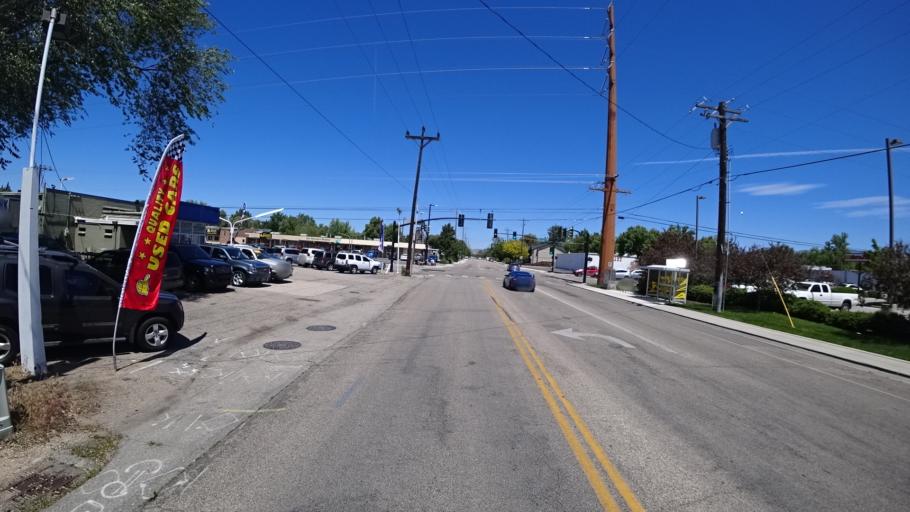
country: US
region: Idaho
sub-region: Ada County
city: Garden City
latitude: 43.5893
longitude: -116.2336
